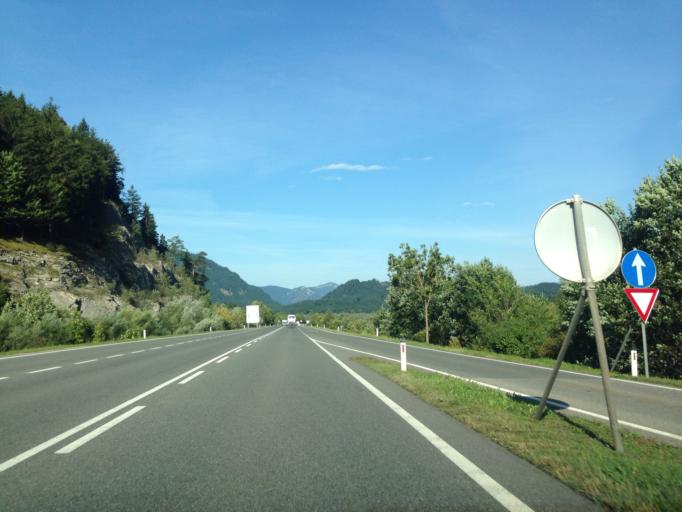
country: AT
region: Tyrol
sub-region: Politischer Bezirk Reutte
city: Pflach
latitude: 47.5255
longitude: 10.7003
